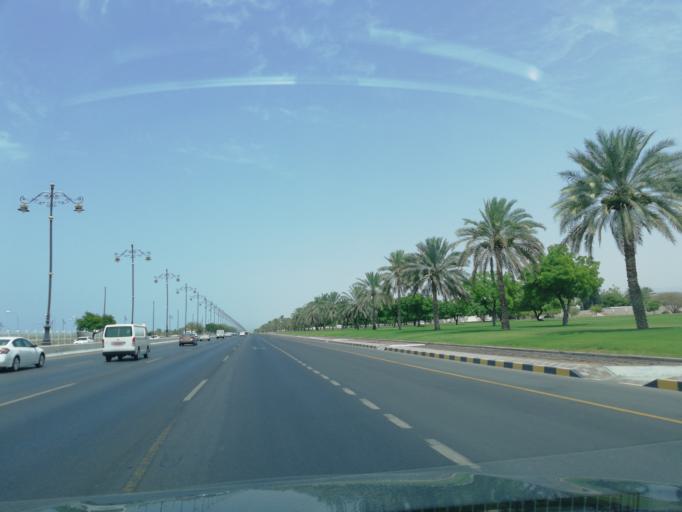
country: OM
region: Muhafazat Masqat
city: As Sib al Jadidah
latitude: 23.5835
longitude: 58.2737
